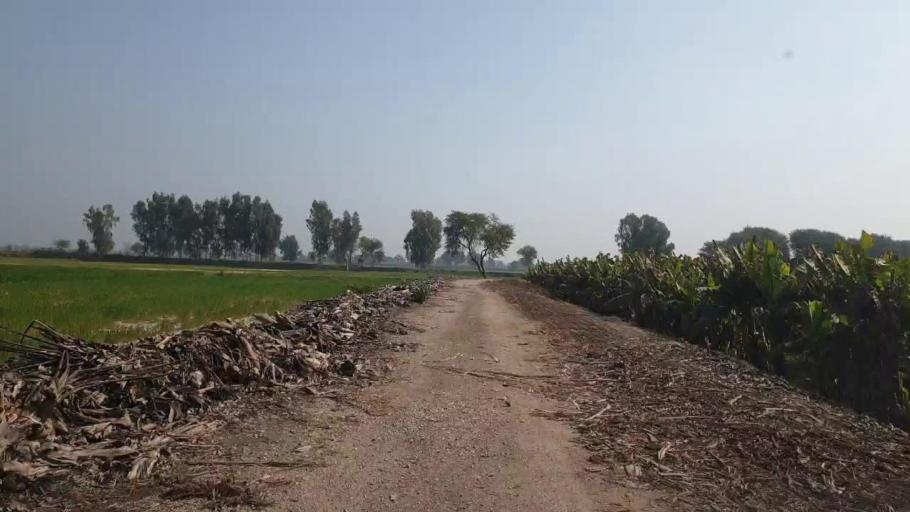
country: PK
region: Sindh
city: Bhit Shah
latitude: 25.7719
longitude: 68.5062
